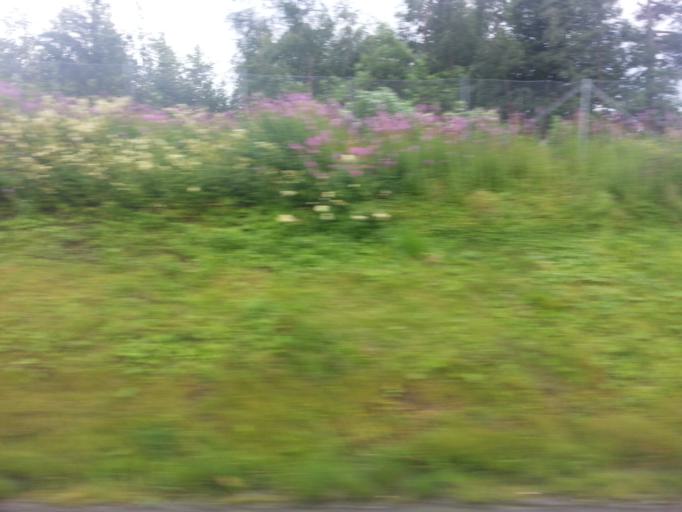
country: NO
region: Sor-Trondelag
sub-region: Malvik
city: Malvik
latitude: 63.4266
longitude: 10.6676
